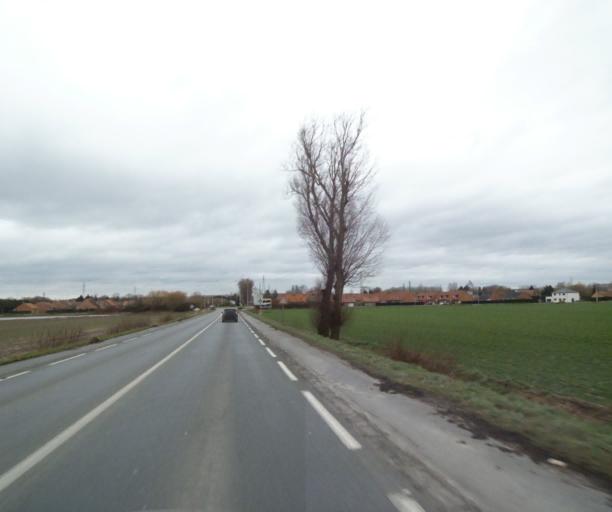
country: FR
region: Nord-Pas-de-Calais
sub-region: Departement du Nord
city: Saint-Saulve
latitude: 50.3795
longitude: 3.5624
